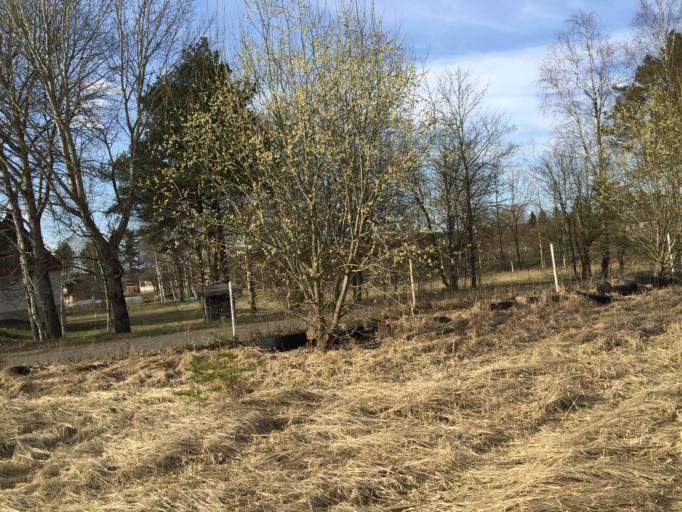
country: LV
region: Ogre
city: Ogre
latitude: 56.8087
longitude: 24.6470
